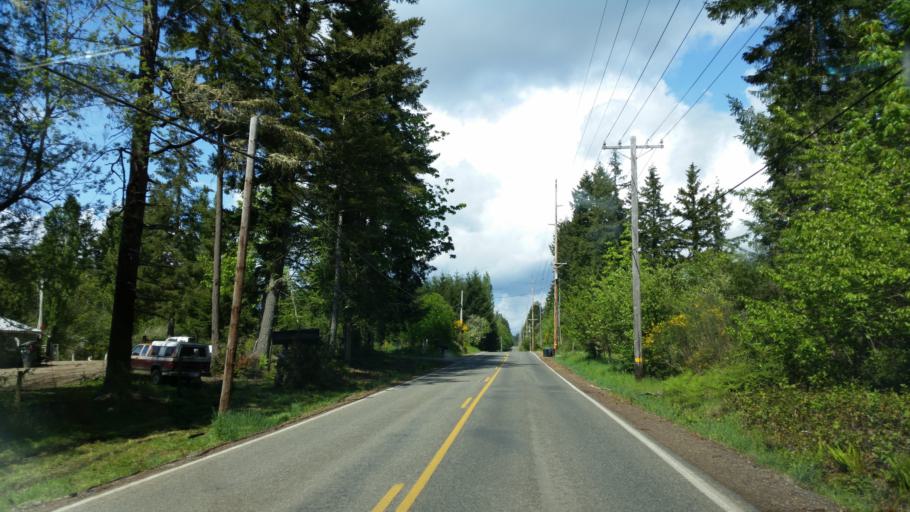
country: US
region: Washington
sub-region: Pierce County
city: Home
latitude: 47.3020
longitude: -122.7698
